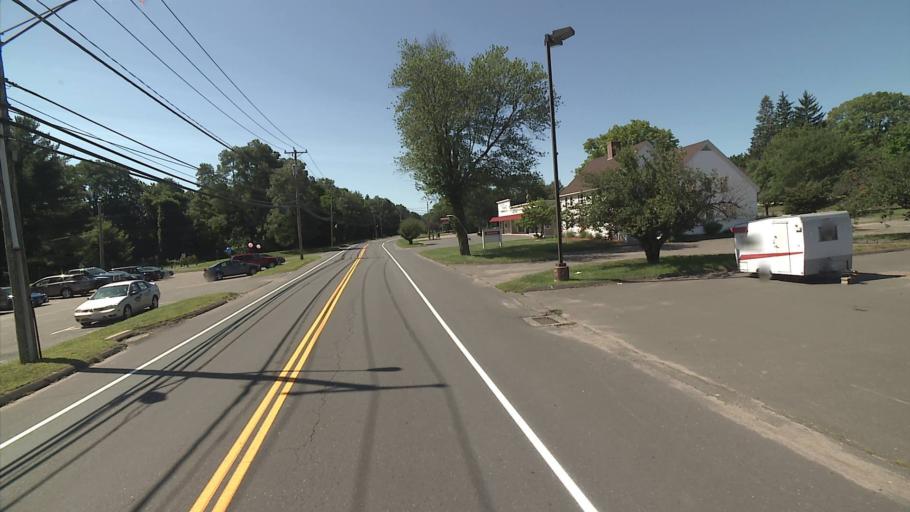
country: US
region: Connecticut
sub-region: Hartford County
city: Tariffville
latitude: 41.9001
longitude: -72.7865
